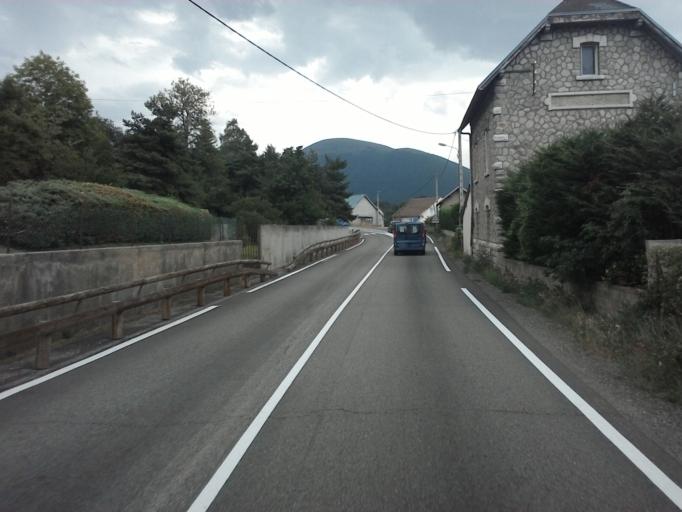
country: FR
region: Rhone-Alpes
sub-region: Departement de l'Isere
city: La Mure
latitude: 44.8763
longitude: 5.8324
